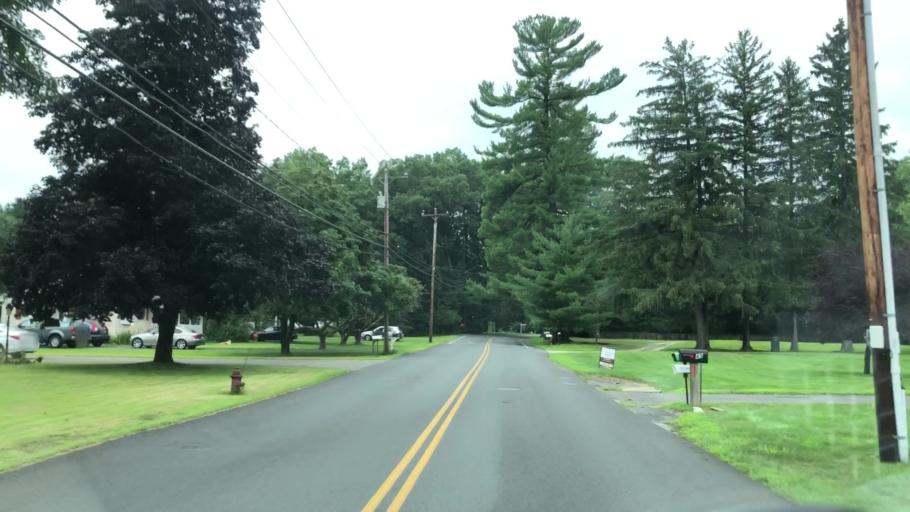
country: US
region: Massachusetts
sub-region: Hampshire County
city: Easthampton
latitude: 42.2720
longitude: -72.6991
